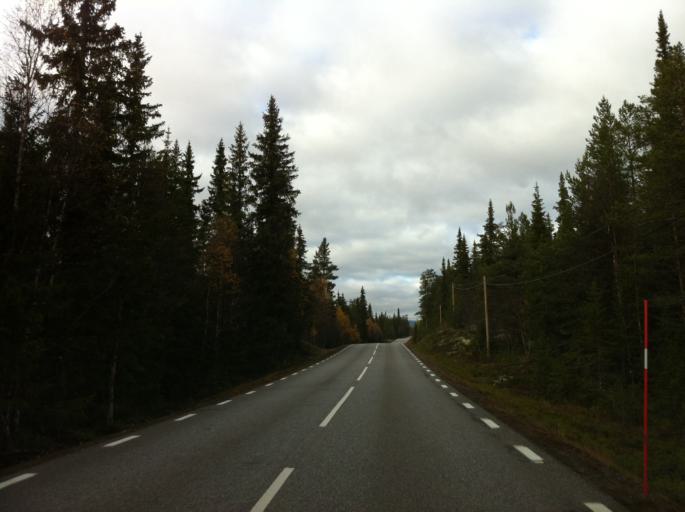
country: NO
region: Hedmark
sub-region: Engerdal
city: Engerdal
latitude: 61.9978
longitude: 12.4583
